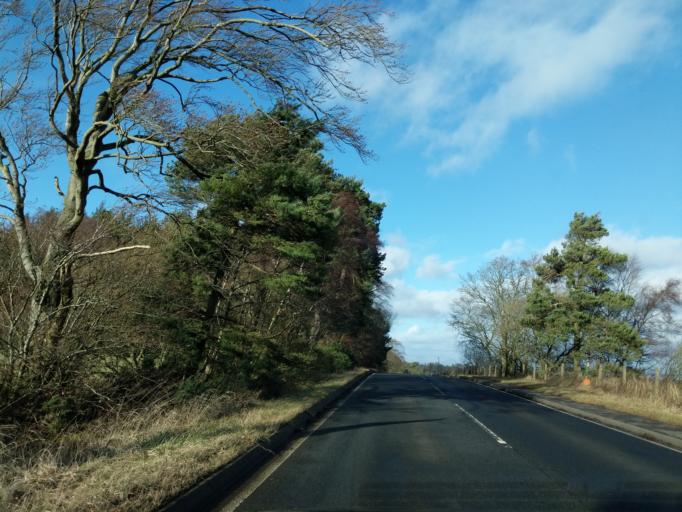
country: GB
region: Scotland
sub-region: West Lothian
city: Kirknewton
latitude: 55.8720
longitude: -3.4072
